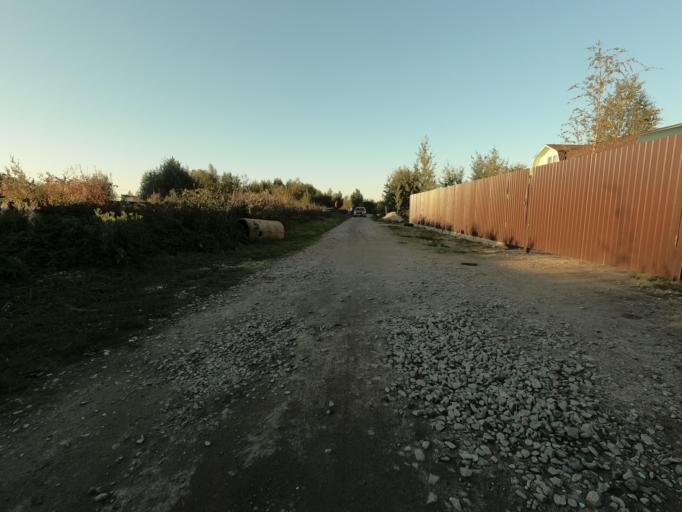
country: RU
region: Leningrad
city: Nikol'skoye
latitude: 59.7060
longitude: 30.7969
